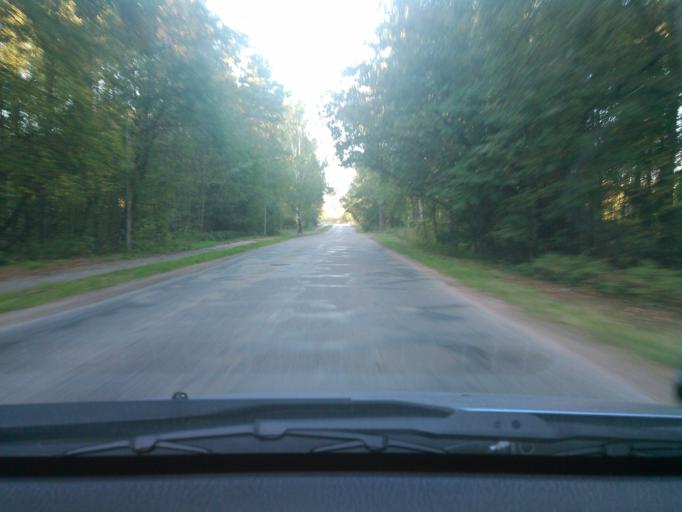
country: LV
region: Adazi
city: Adazi
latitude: 57.0859
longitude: 24.3449
